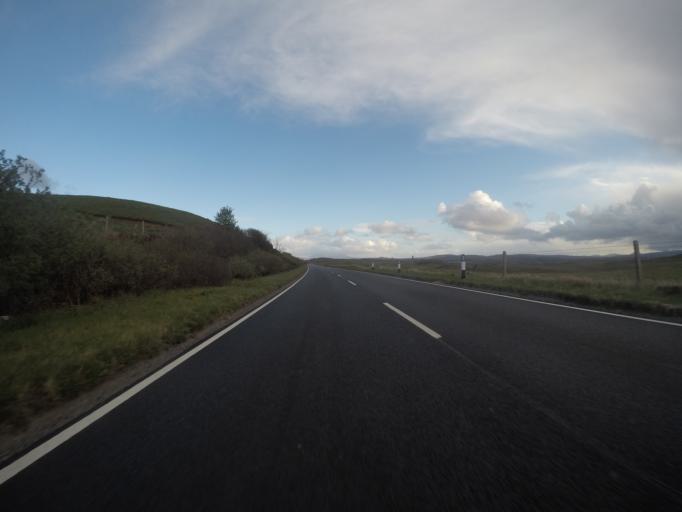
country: GB
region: Scotland
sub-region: Highland
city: Portree
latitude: 57.5422
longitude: -6.3647
